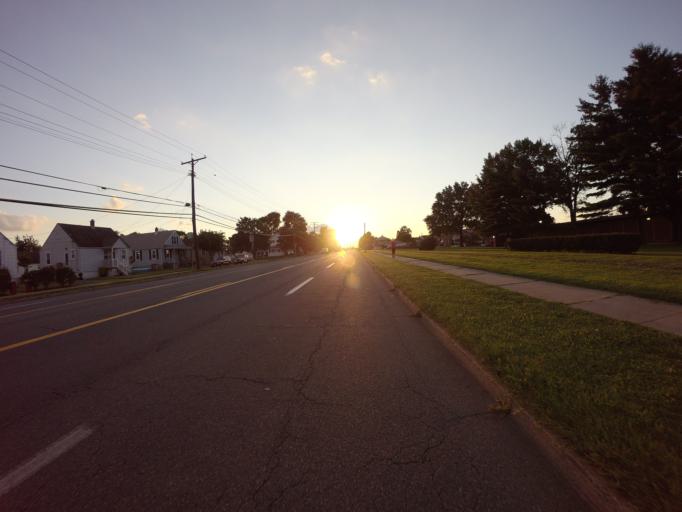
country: US
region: Maryland
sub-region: Baltimore County
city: Dundalk
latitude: 39.2646
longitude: -76.4891
